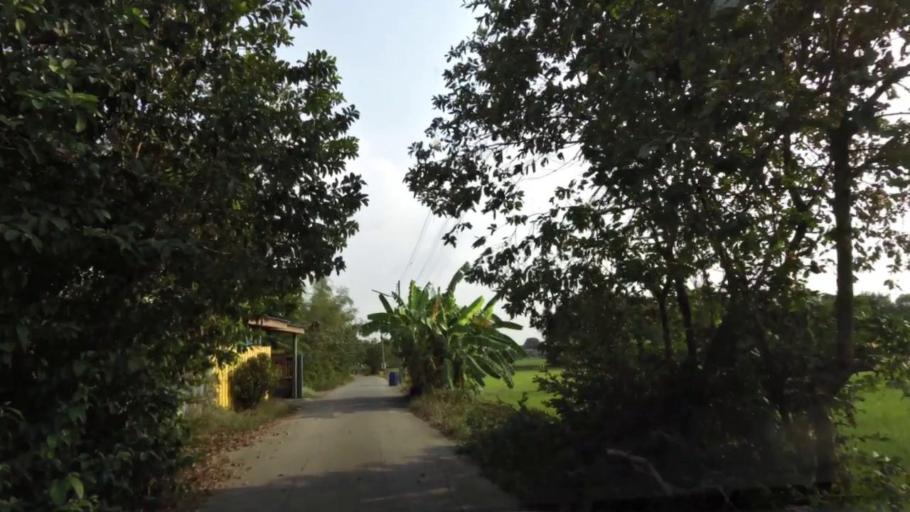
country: TH
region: Phra Nakhon Si Ayutthaya
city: Phra Nakhon Si Ayutthaya
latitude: 14.3287
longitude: 100.5665
